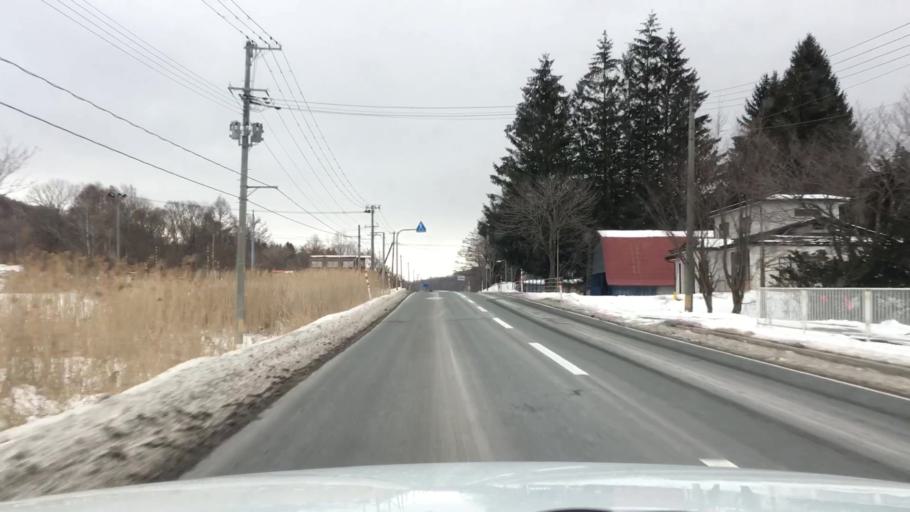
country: JP
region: Iwate
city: Morioka-shi
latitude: 39.6433
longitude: 141.3983
